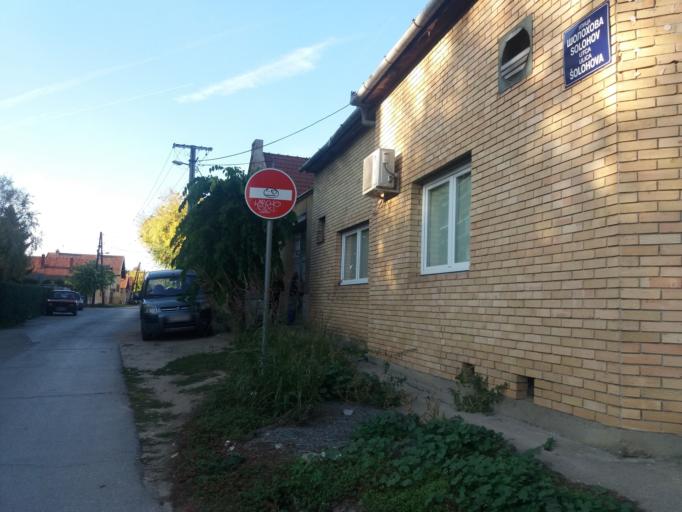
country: RS
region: Autonomna Pokrajina Vojvodina
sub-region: Severnobacki Okrug
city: Subotica
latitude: 46.0910
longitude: 19.6737
